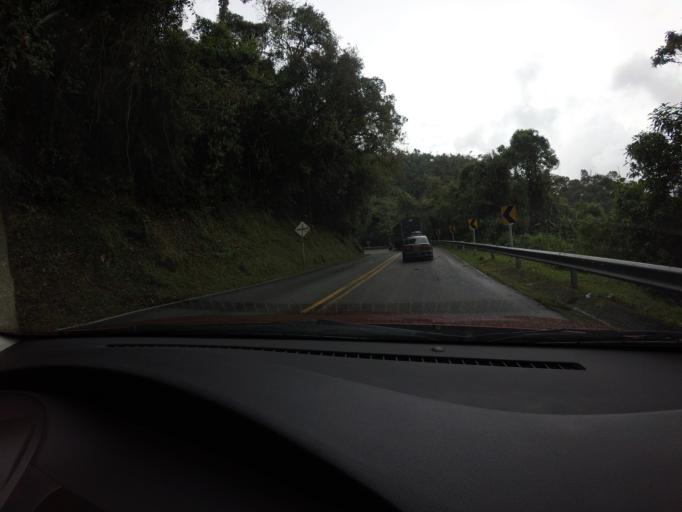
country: CO
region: Tolima
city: Herveo
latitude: 5.1403
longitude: -75.1596
